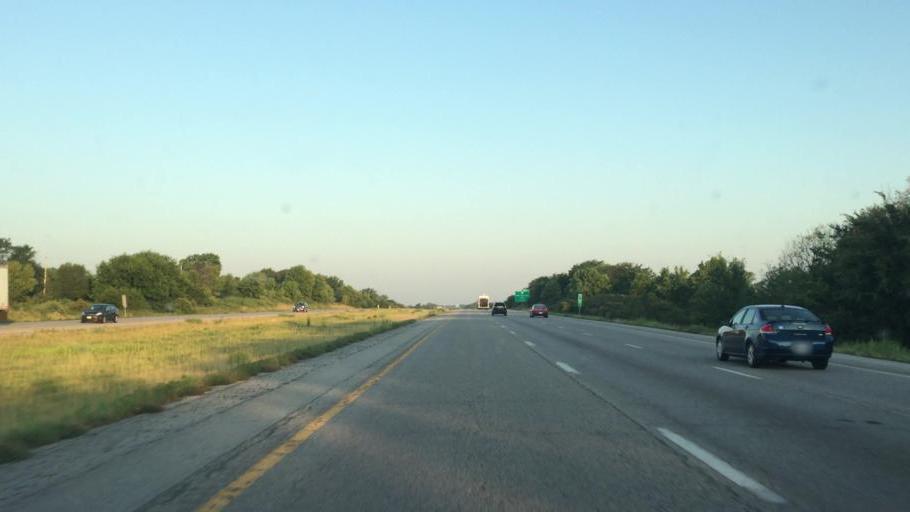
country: US
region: Missouri
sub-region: Clay County
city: Smithville
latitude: 39.3075
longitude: -94.6314
